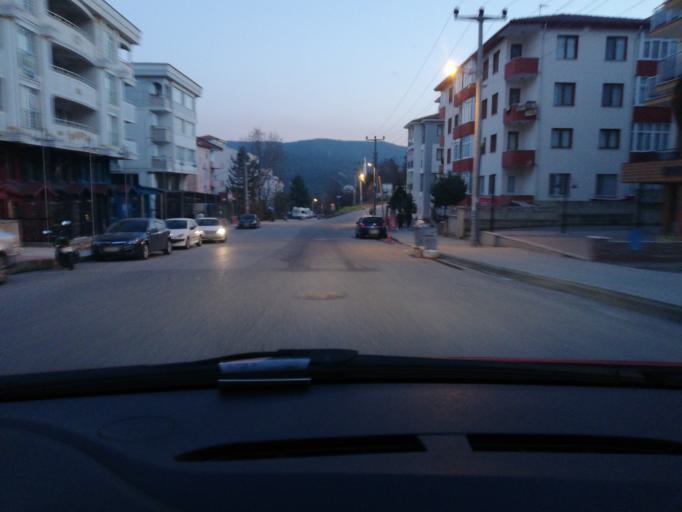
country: TR
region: Karabuk
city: Safranbolu
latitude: 41.2202
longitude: 32.6727
